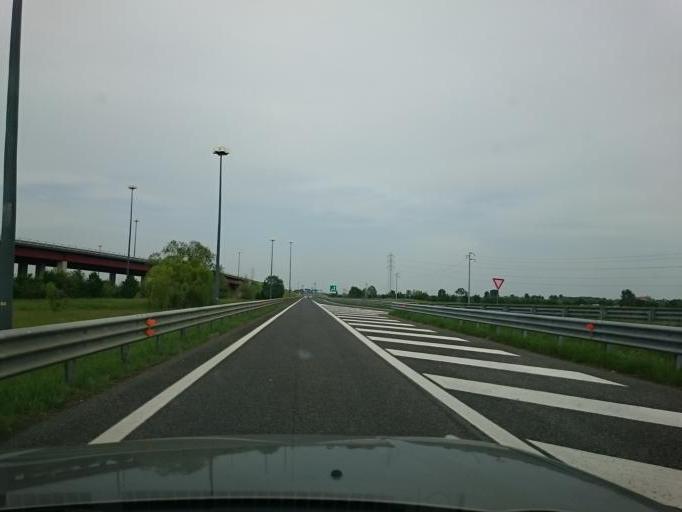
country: IT
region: Veneto
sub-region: Provincia di Venezia
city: Dese
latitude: 45.5337
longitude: 12.2803
